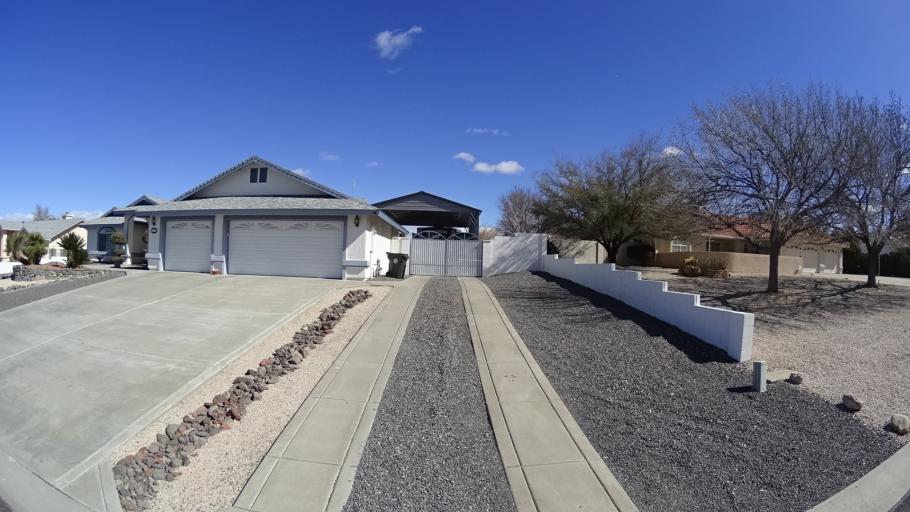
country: US
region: Arizona
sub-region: Mohave County
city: Kingman
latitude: 35.2022
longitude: -113.9647
